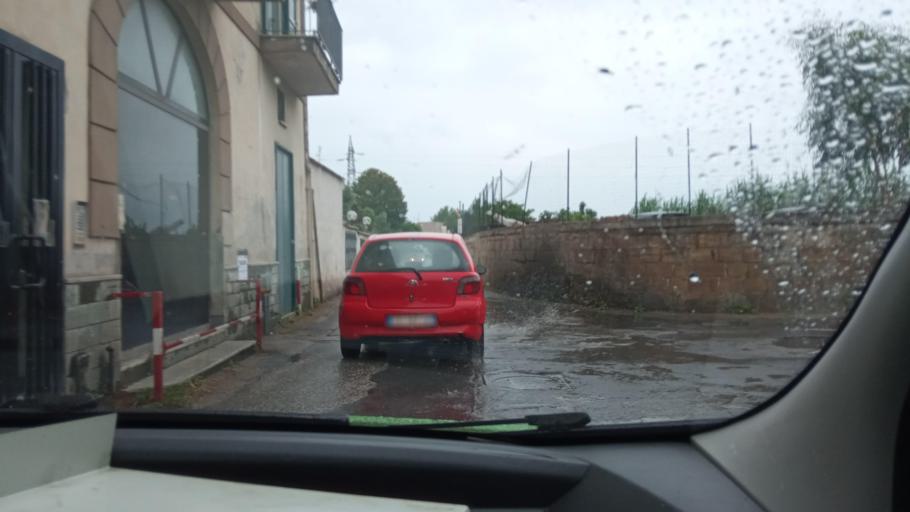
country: IT
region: Campania
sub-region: Provincia di Napoli
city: Quarto
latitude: 40.8426
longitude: 14.1178
